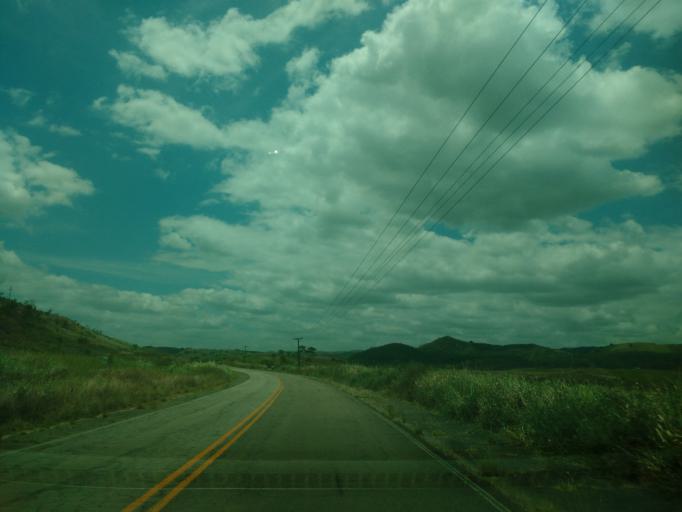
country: BR
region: Alagoas
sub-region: Uniao Dos Palmares
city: Uniao dos Palmares
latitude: -9.1407
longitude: -36.0914
